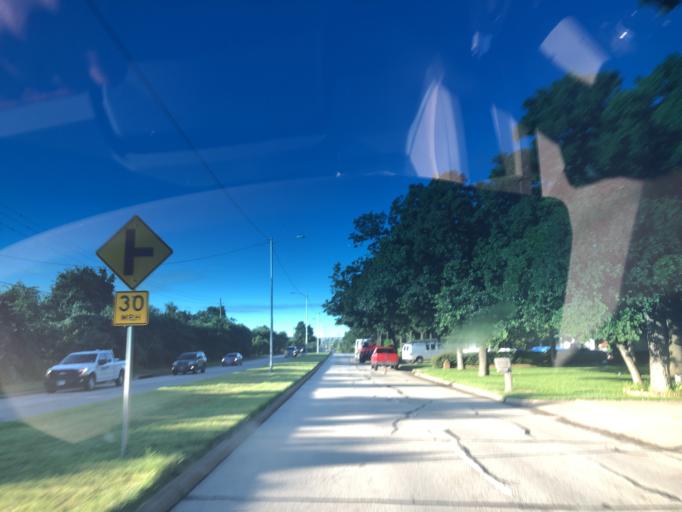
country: US
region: Texas
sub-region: Dallas County
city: Grand Prairie
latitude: 32.7780
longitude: -97.0285
